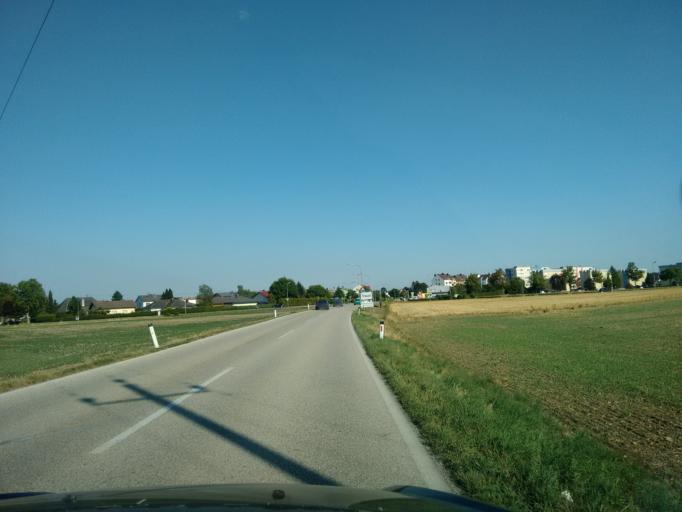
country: AT
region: Upper Austria
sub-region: Politischer Bezirk Linz-Land
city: Traun
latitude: 48.2211
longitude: 14.2175
